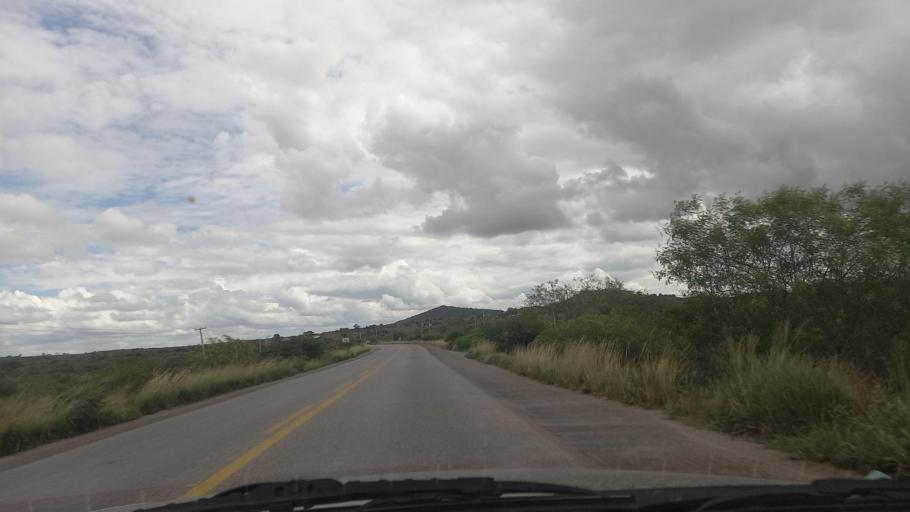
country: BR
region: Pernambuco
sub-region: Cachoeirinha
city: Cachoeirinha
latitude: -8.3368
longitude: -36.1563
